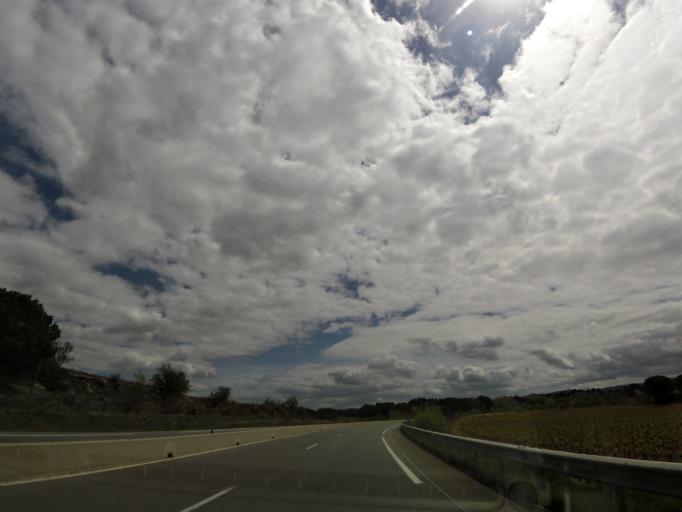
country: FR
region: Languedoc-Roussillon
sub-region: Departement de l'Aude
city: Trebes
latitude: 43.2014
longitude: 2.4189
